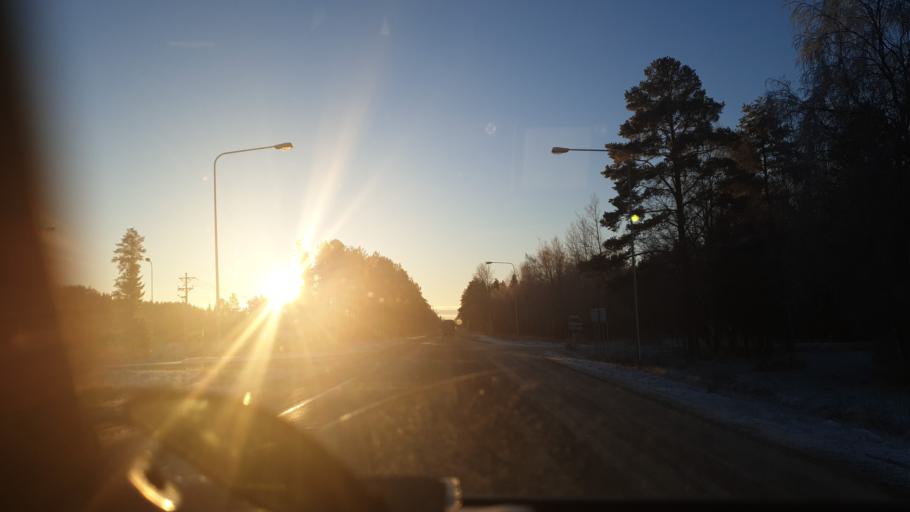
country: FI
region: Northern Ostrobothnia
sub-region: Ylivieska
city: Kalajoki
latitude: 64.2784
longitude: 23.9486
